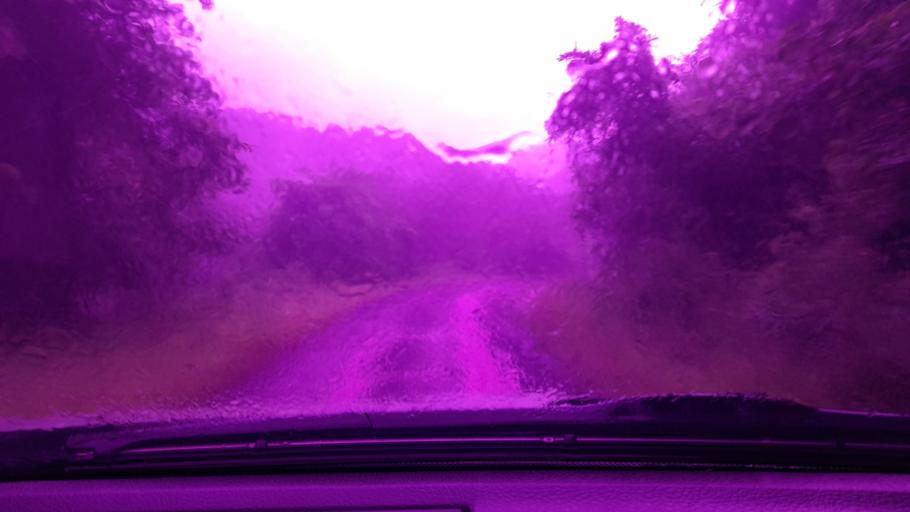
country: ET
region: Oromiya
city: Metu
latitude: 8.4801
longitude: 35.6464
